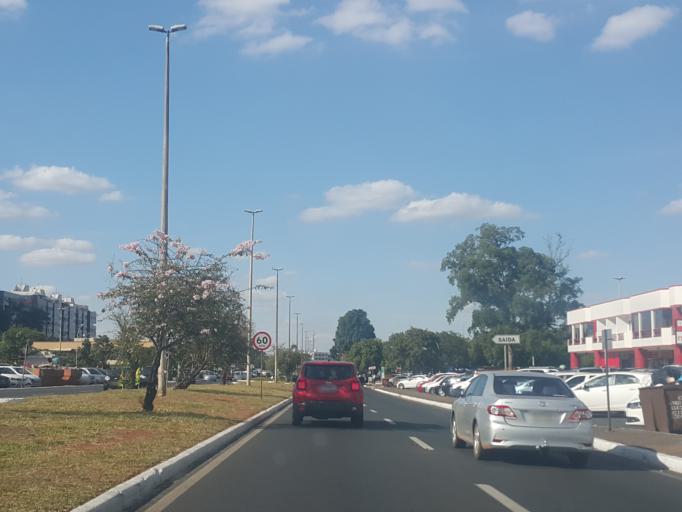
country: BR
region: Federal District
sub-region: Brasilia
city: Brasilia
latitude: -15.7996
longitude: -47.9229
